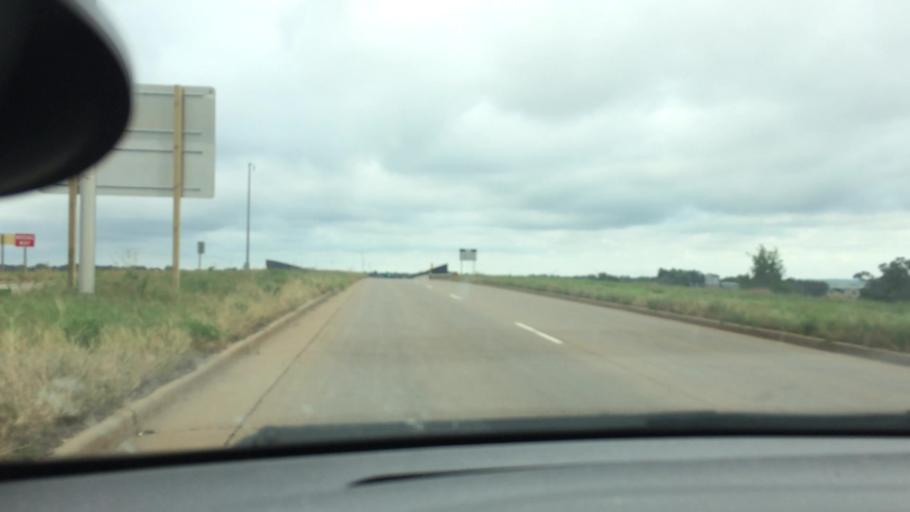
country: US
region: Wisconsin
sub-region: Chippewa County
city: Lake Hallie
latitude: 44.8815
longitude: -91.4118
